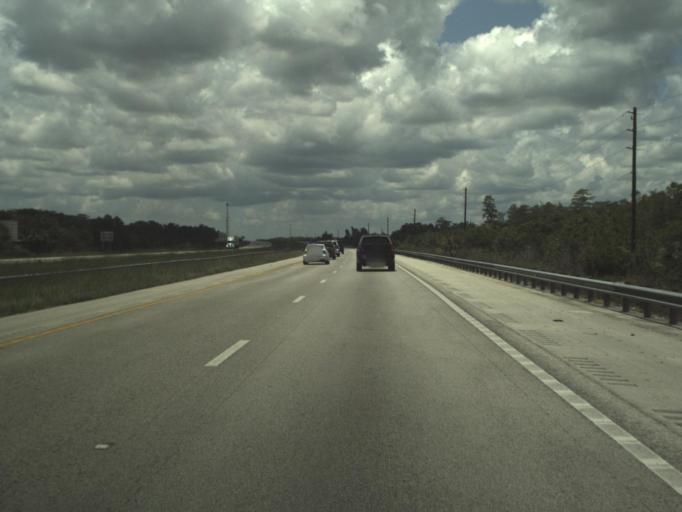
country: US
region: Florida
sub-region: Broward County
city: Weston
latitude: 26.1726
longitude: -80.8676
